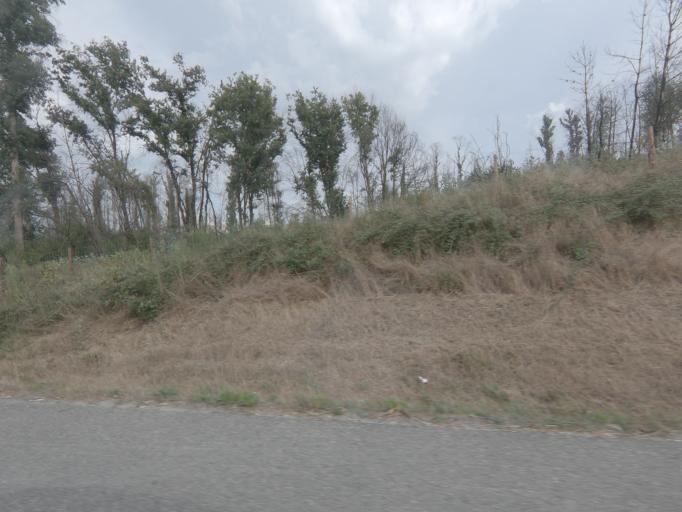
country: PT
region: Viseu
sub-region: Santa Comba Dao
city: Santa Comba Dao
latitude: 40.4237
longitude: -8.1193
